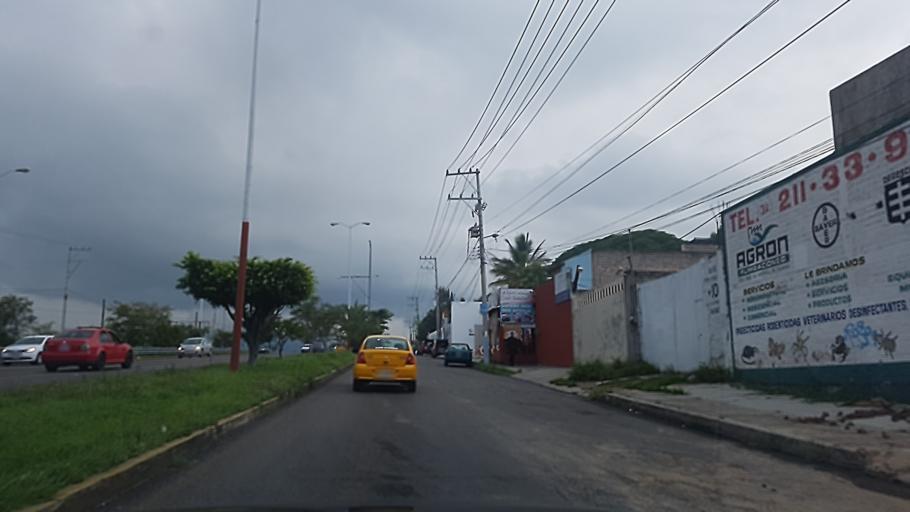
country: MX
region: Nayarit
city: Xalisco
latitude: 21.4657
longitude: -104.8889
